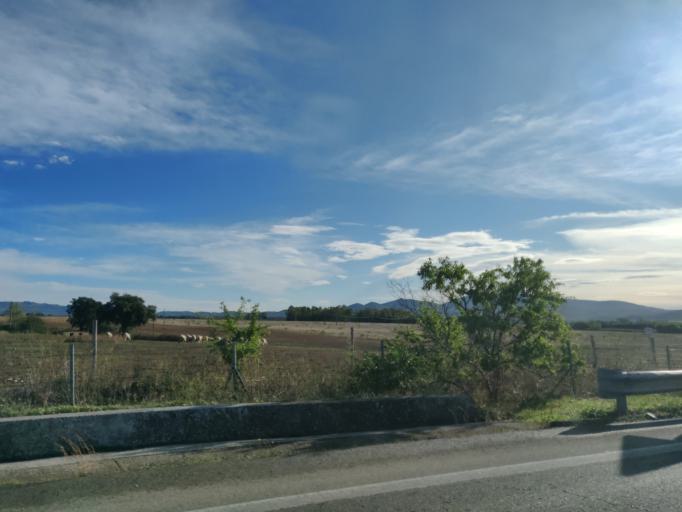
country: IT
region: Tuscany
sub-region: Provincia di Grosseto
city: Braccagni
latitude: 42.9011
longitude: 11.0455
